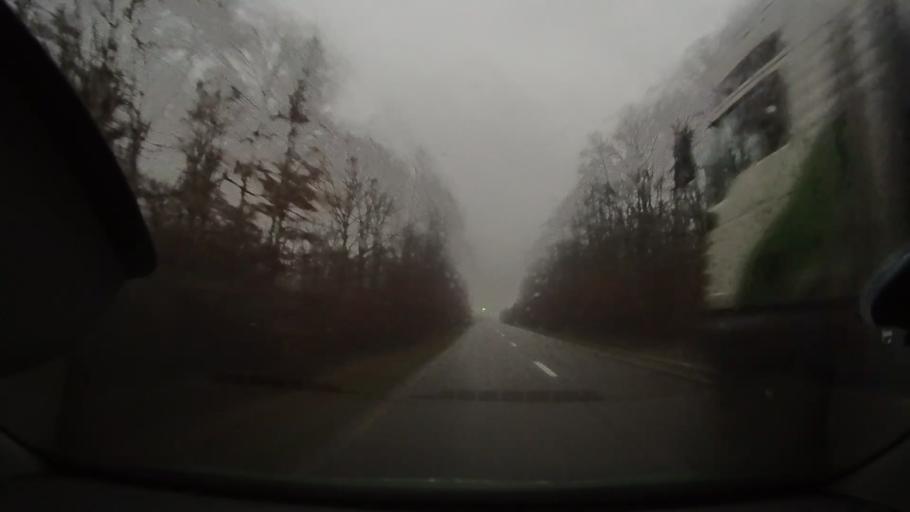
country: RO
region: Arad
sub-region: Comuna Beliu
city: Beliu
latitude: 46.5032
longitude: 21.9729
